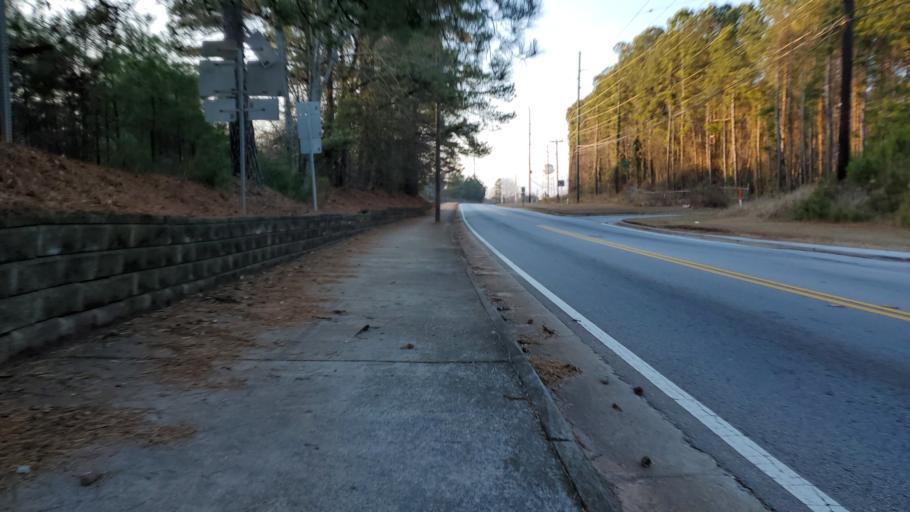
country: US
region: Georgia
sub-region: DeKalb County
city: Stone Mountain
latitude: 33.8147
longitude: -84.1791
